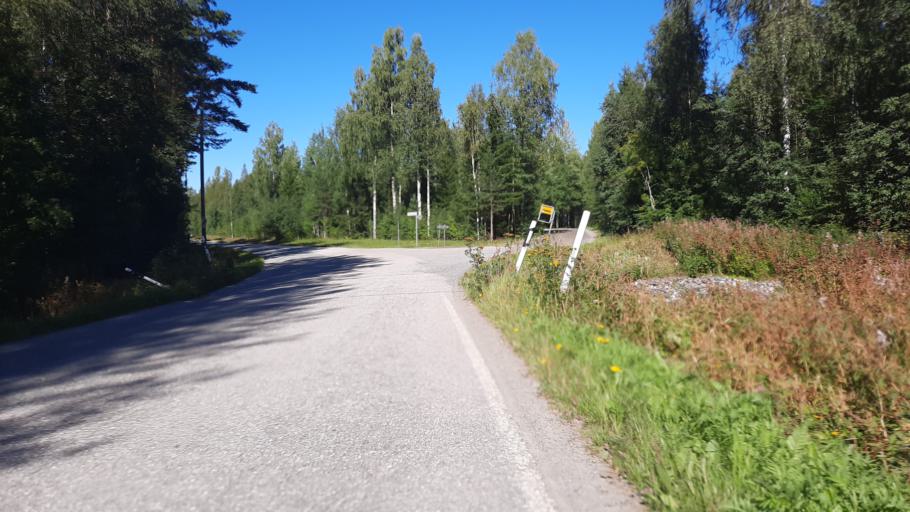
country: FI
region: North Karelia
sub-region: Joensuu
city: Joensuu
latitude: 62.6294
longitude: 29.7357
